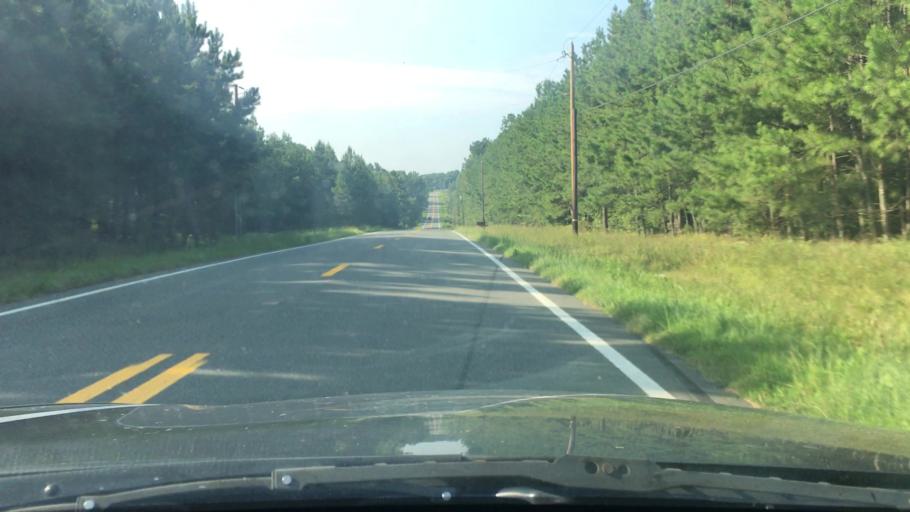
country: US
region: North Carolina
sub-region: Alamance County
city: Green Level
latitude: 36.2389
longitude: -79.3225
